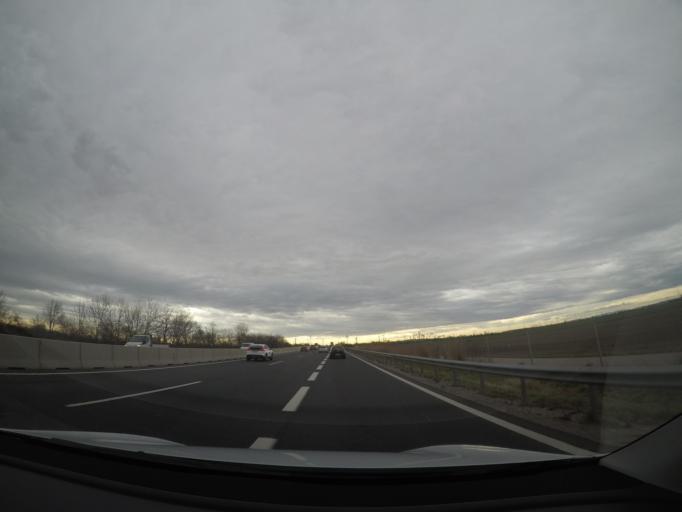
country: AT
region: Lower Austria
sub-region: Politischer Bezirk Modling
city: Munchendorf
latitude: 48.0191
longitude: 16.3581
